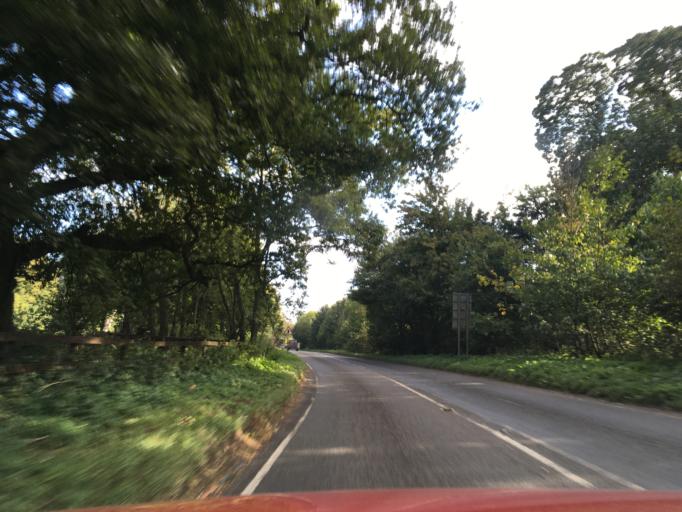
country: GB
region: England
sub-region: Hampshire
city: Basingstoke
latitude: 51.2172
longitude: -1.0598
